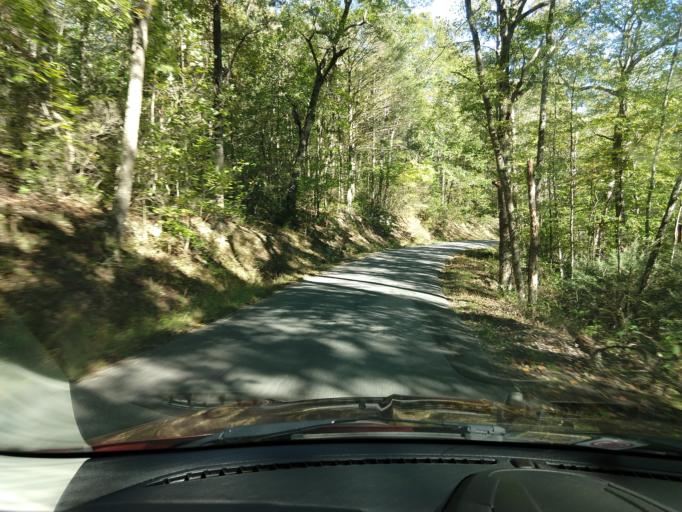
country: US
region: Virginia
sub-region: Alleghany County
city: Clifton Forge
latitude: 37.8584
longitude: -79.8740
